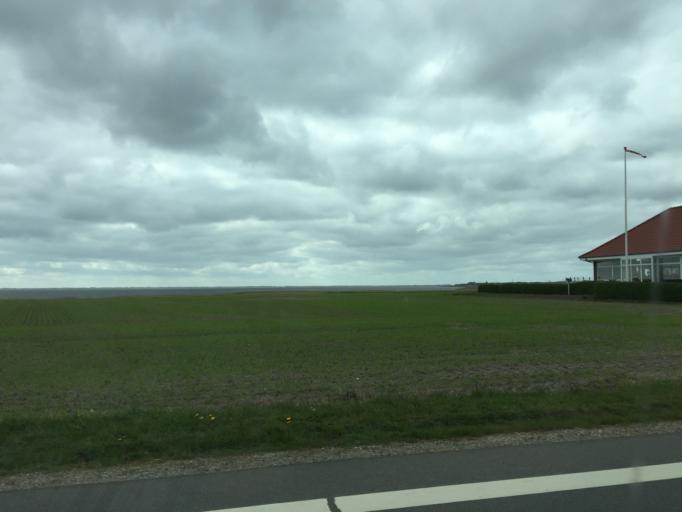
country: DK
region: Central Jutland
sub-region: Ringkobing-Skjern Kommune
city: Ringkobing
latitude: 56.0538
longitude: 8.3117
